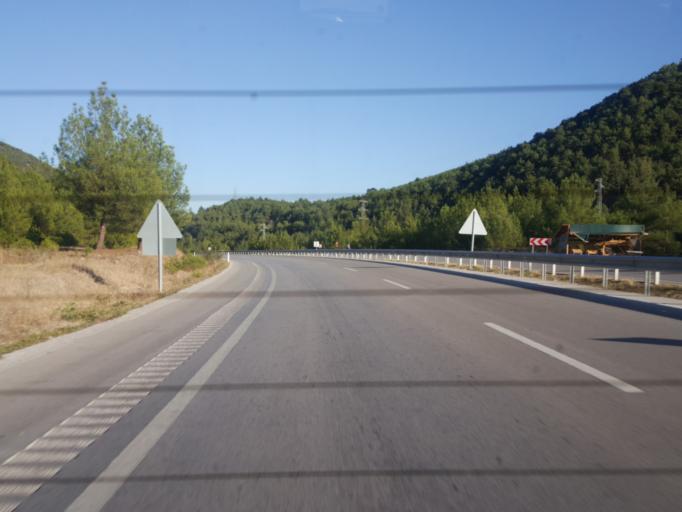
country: TR
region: Amasya
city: Akdag
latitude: 40.7522
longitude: 36.0753
